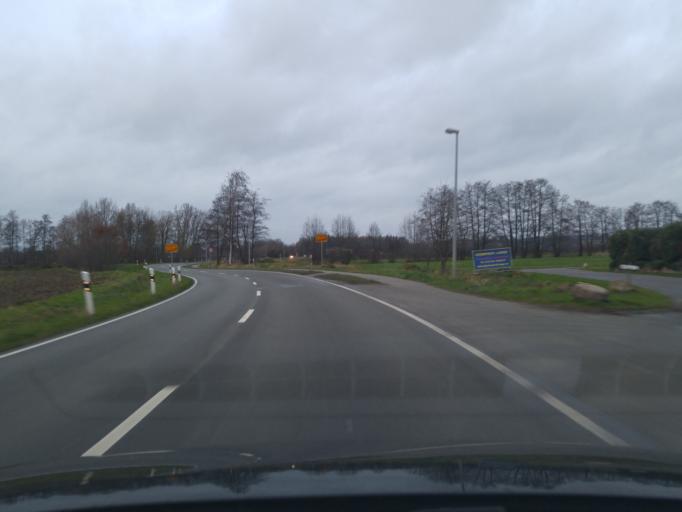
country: DE
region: Lower Saxony
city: Hittbergen
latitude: 53.3487
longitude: 10.5689
